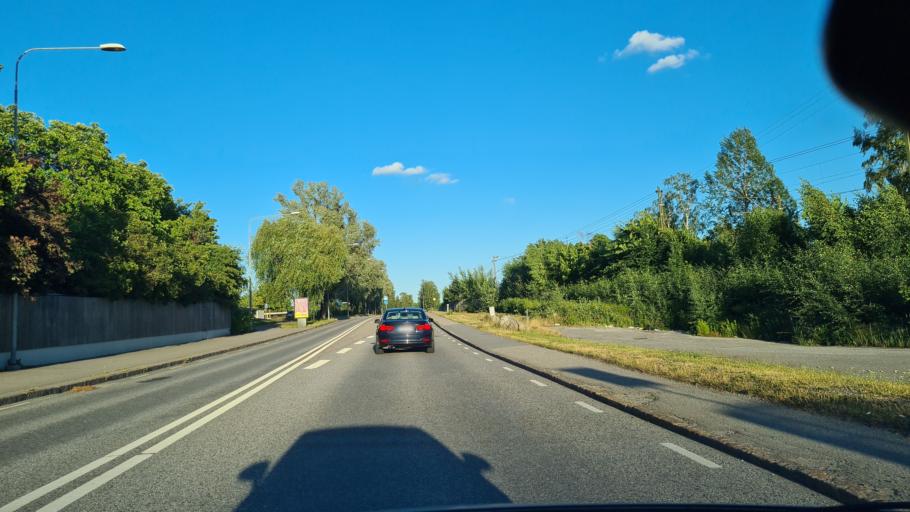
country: SE
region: Stockholm
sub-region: Sodertalje Kommun
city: Soedertaelje
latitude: 59.1875
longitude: 17.6532
